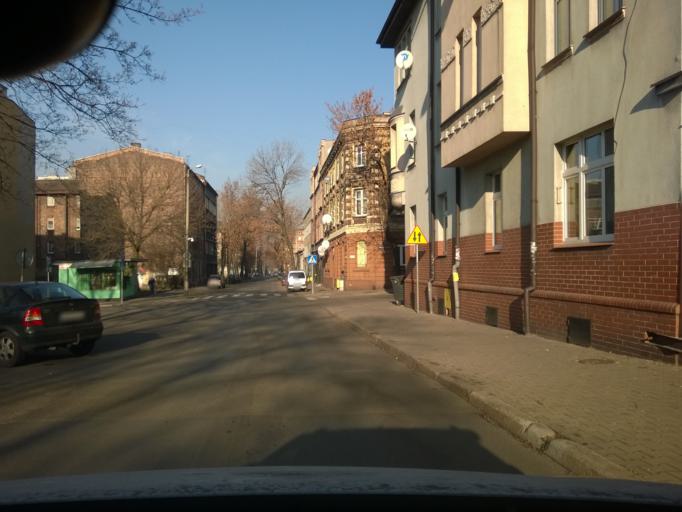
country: PL
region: Silesian Voivodeship
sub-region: Chorzow
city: Chorzow
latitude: 50.3061
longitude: 18.9489
